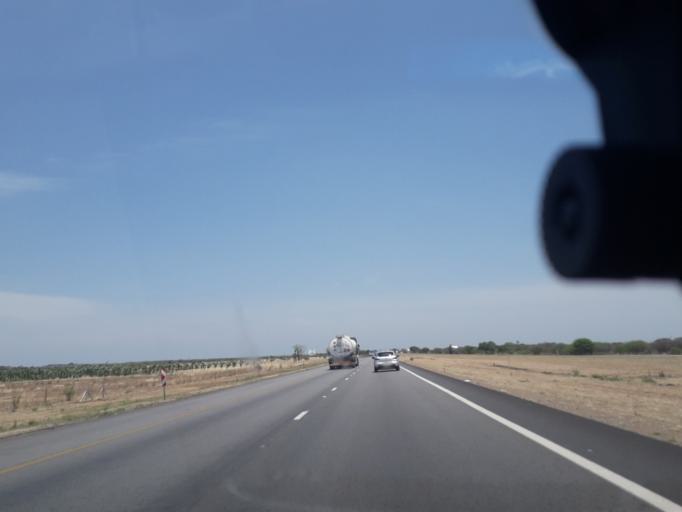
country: ZA
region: Limpopo
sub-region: Waterberg District Municipality
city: Bela-Bela
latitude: -25.1028
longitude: 28.3134
